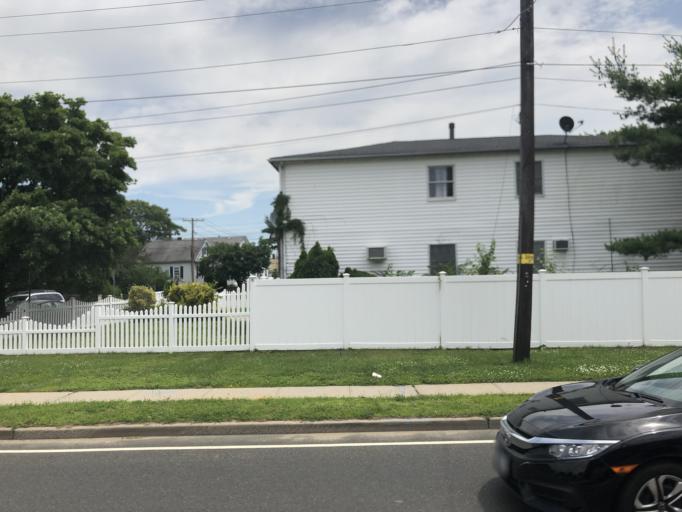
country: US
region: New York
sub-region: Nassau County
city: Elmont
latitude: 40.7055
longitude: -73.7107
